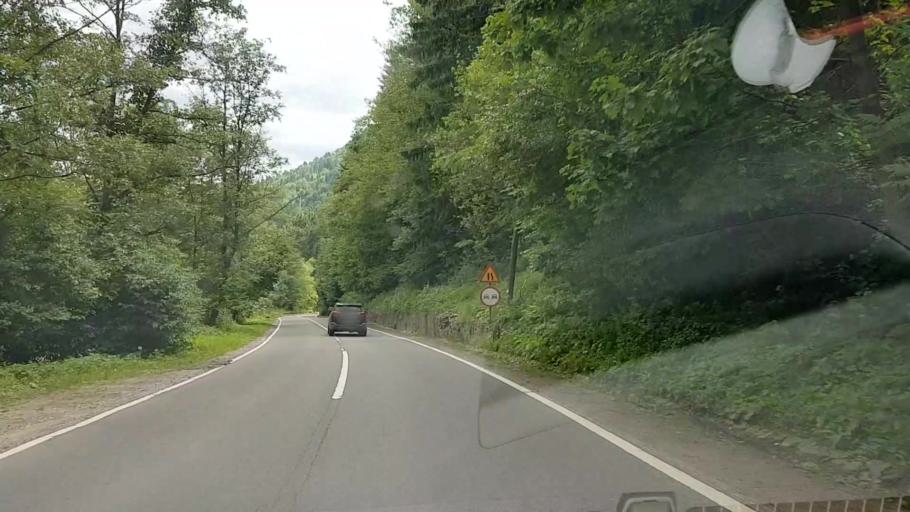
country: RO
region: Neamt
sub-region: Comuna Farcasa
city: Farcasa
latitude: 47.1384
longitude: 25.8610
